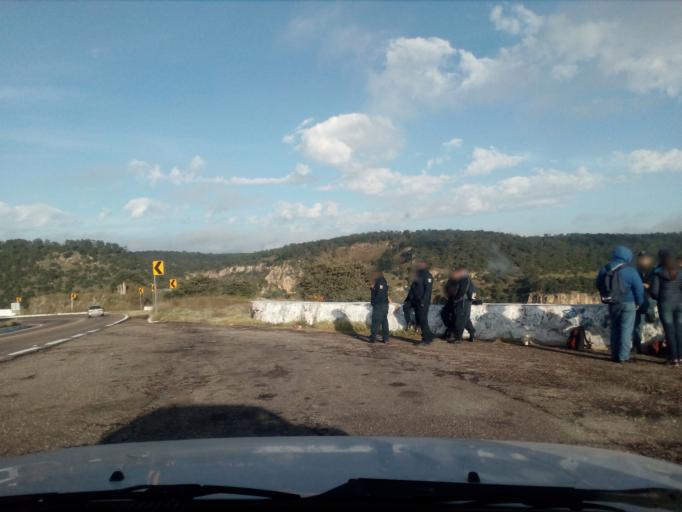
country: MX
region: Durango
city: Victoria de Durango
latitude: 23.9562
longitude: -104.8500
